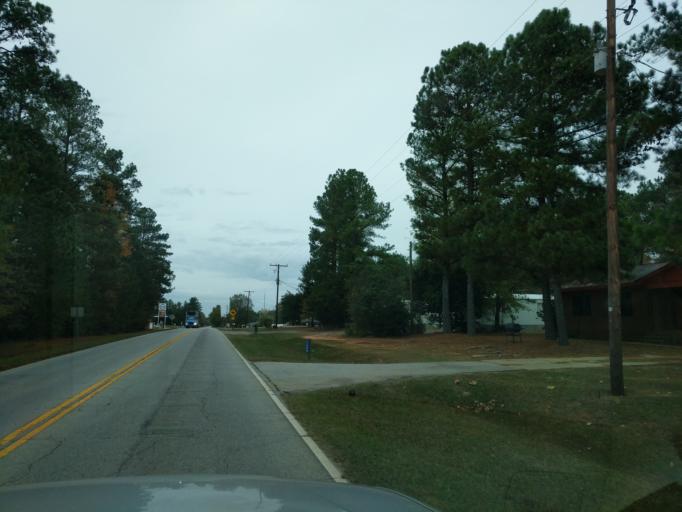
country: US
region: South Carolina
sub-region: Saluda County
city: Saluda
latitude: 34.0774
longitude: -81.7587
